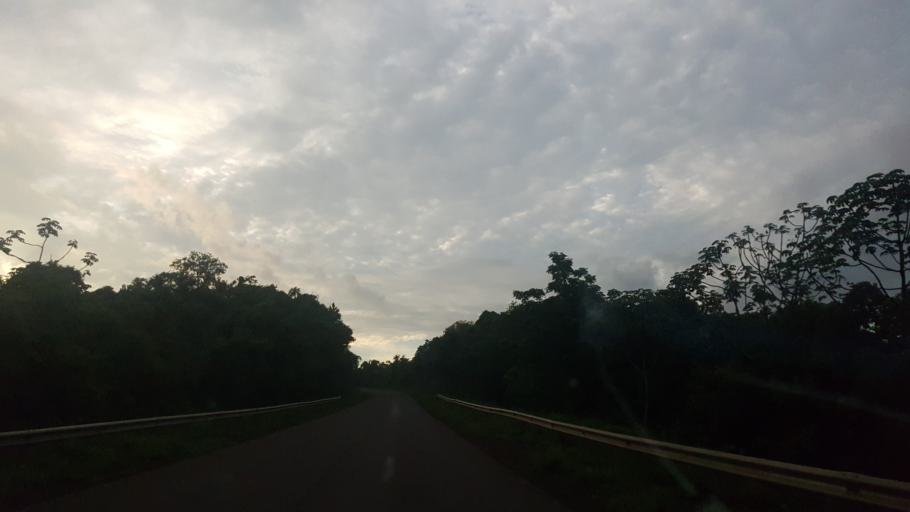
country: AR
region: Misiones
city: Dos de Mayo
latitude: -26.9239
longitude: -54.7275
